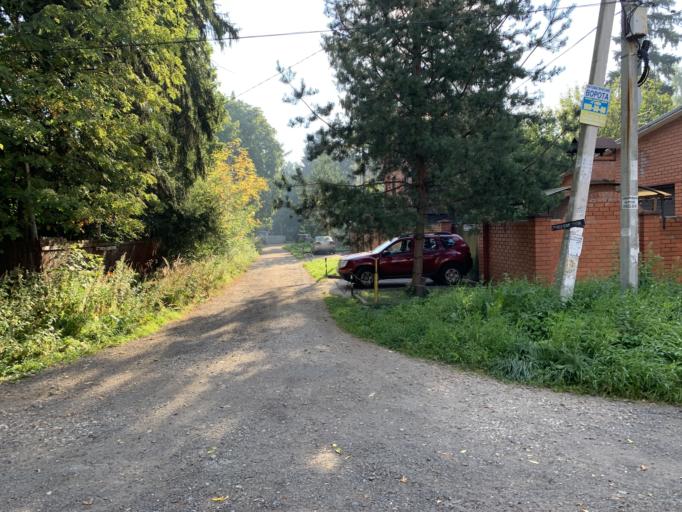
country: RU
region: Moskovskaya
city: Mamontovka
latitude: 55.9786
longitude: 37.8433
